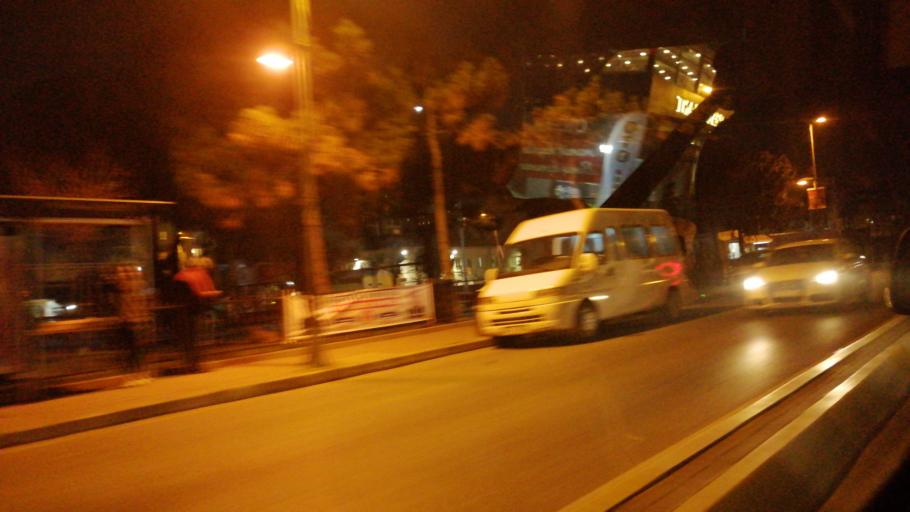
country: TR
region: Istanbul
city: Umraniye
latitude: 41.0154
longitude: 29.1286
